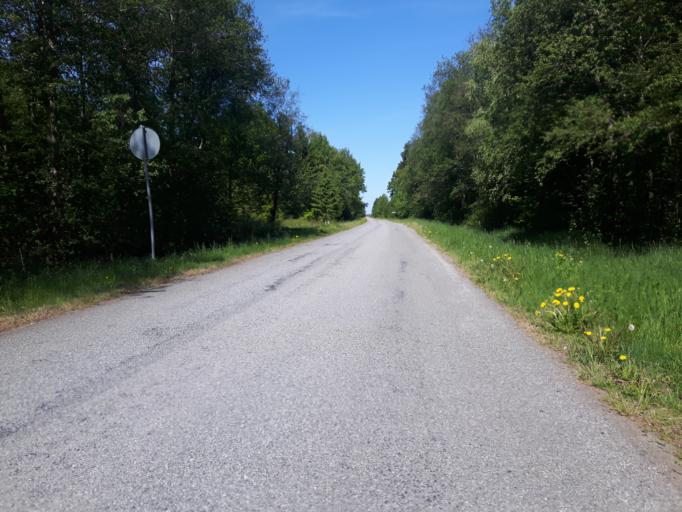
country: EE
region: Ida-Virumaa
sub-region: Aseri vald
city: Aseri
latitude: 59.4527
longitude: 26.8527
